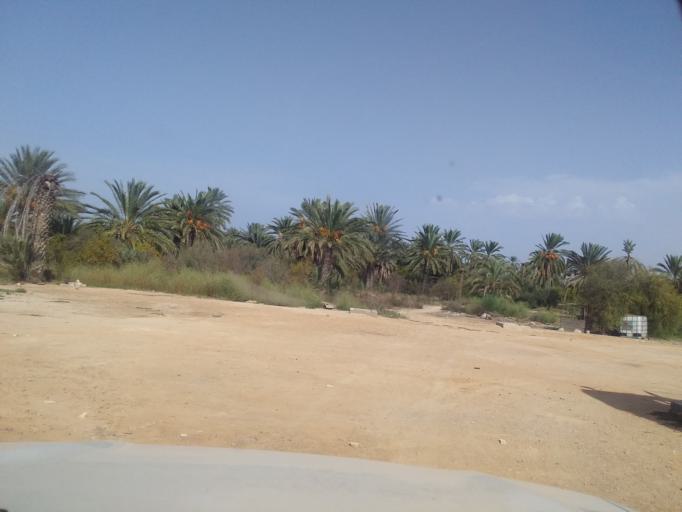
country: TN
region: Qabis
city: Gabes
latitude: 33.6318
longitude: 10.2860
